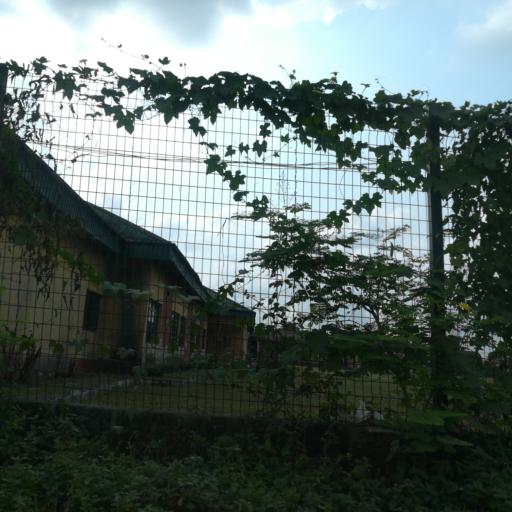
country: NG
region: Rivers
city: Okrika
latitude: 4.7934
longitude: 7.1210
